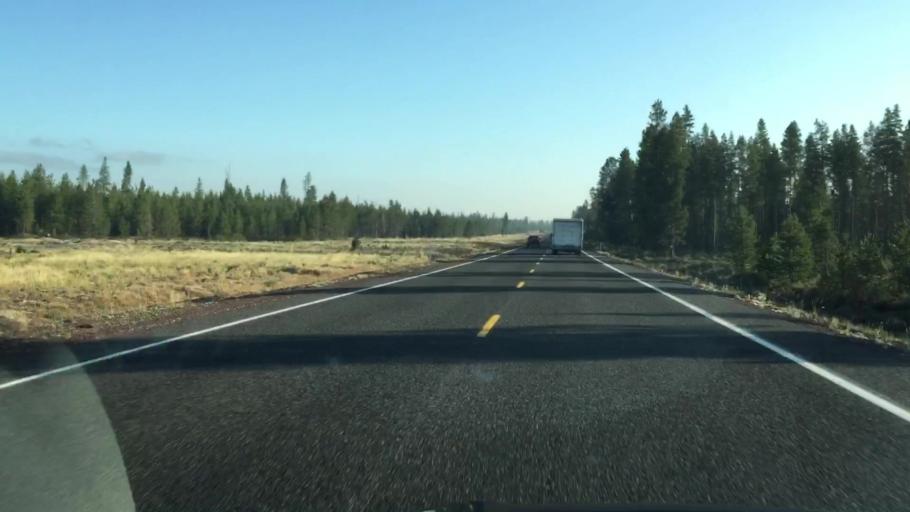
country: US
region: Oregon
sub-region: Deschutes County
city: La Pine
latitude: 43.4353
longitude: -121.7128
